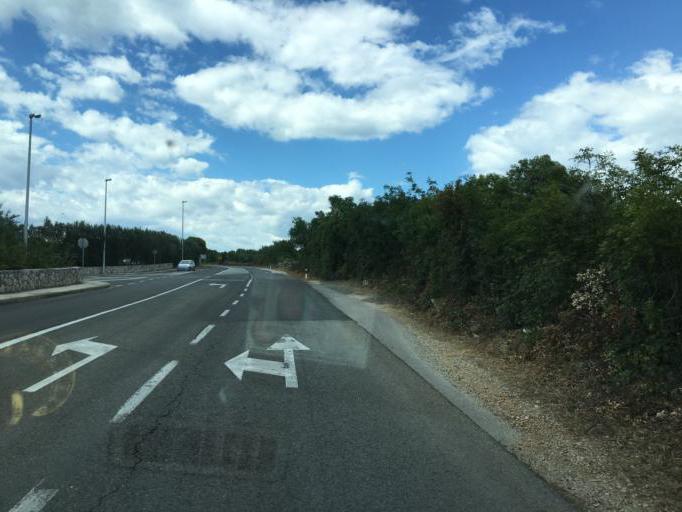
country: HR
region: Primorsko-Goranska
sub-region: Grad Krk
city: Krk
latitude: 45.0374
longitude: 14.5696
